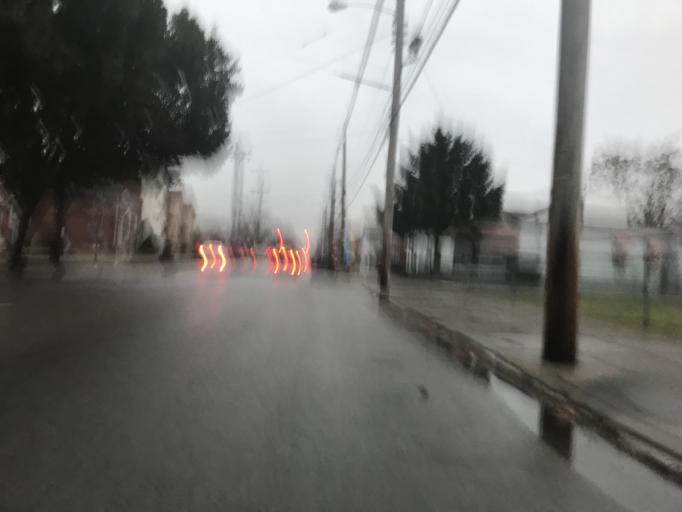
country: US
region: Kentucky
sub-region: Jefferson County
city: Louisville
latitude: 38.2410
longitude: -85.7402
